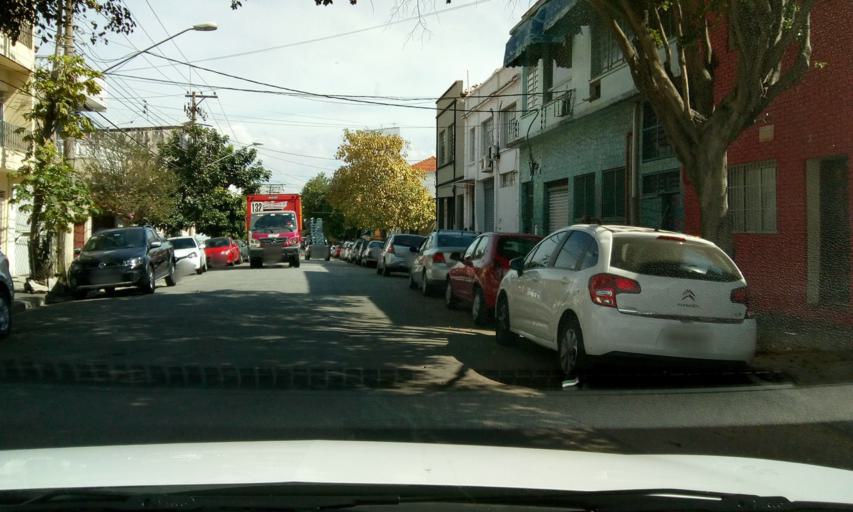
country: BR
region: Sao Paulo
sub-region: Sao Paulo
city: Sao Paulo
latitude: -23.5404
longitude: -46.6032
